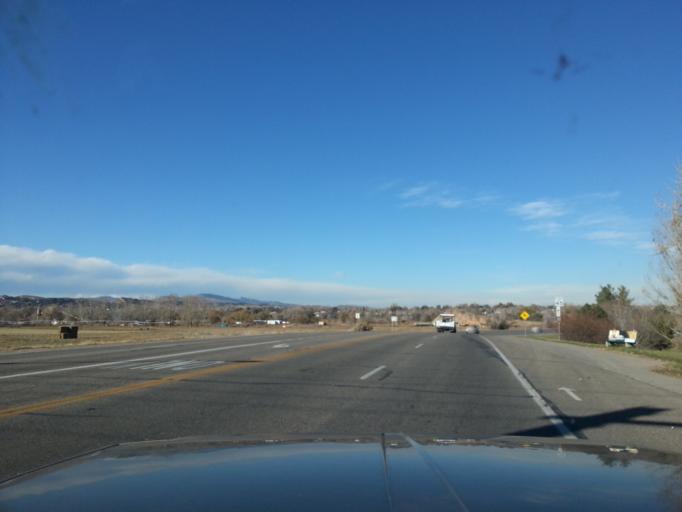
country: US
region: Colorado
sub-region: Larimer County
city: Loveland
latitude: 40.3928
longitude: -105.1159
